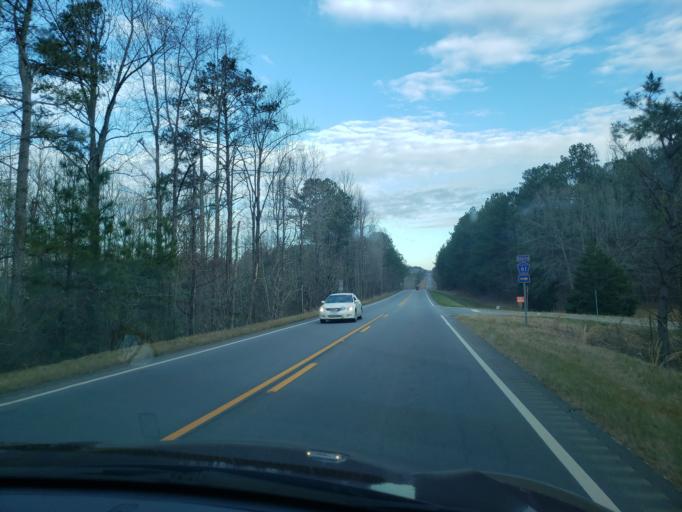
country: US
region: Alabama
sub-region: Randolph County
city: Wedowee
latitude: 33.2331
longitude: -85.4374
